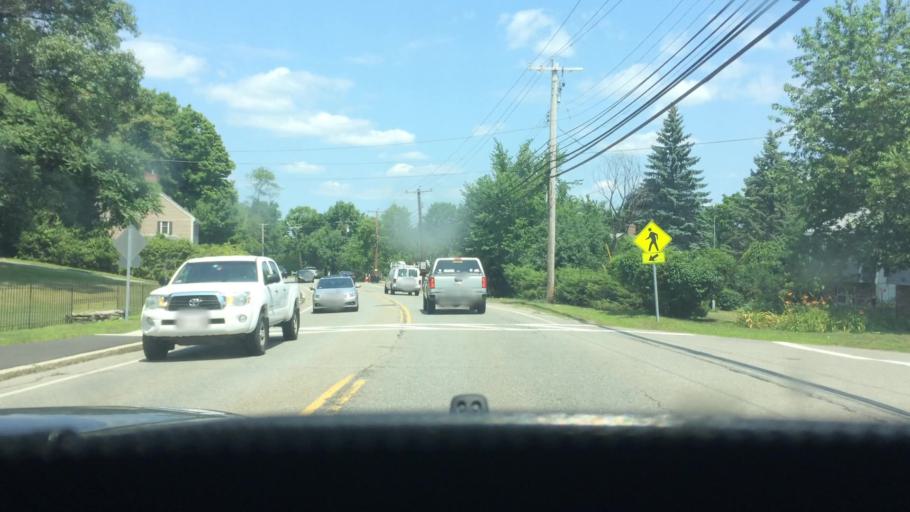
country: US
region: Massachusetts
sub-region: Middlesex County
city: Chelmsford
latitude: 42.6097
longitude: -71.3574
